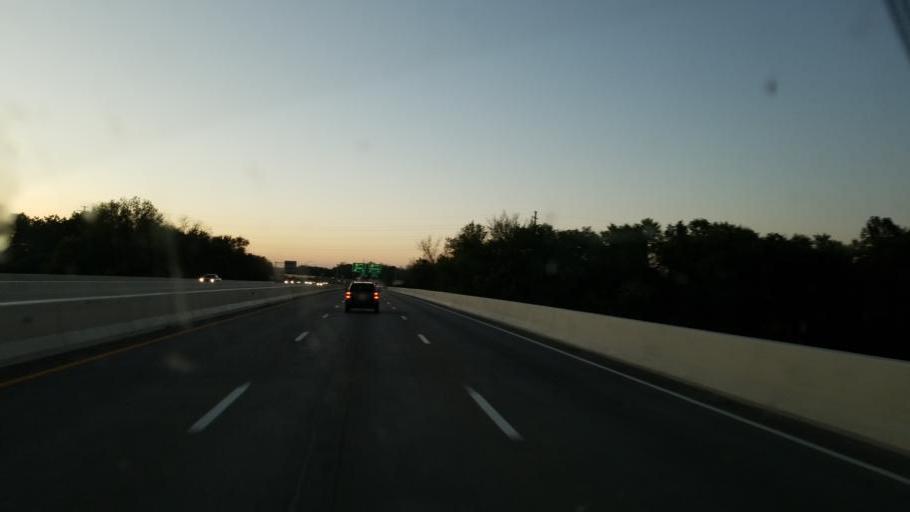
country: US
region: Ohio
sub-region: Ross County
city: Chillicothe
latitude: 39.3455
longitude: -82.9554
